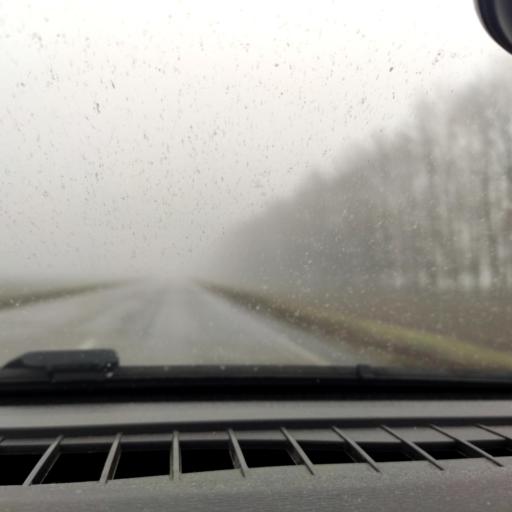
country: RU
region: Belgorod
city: Ilovka
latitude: 50.7453
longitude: 38.7116
